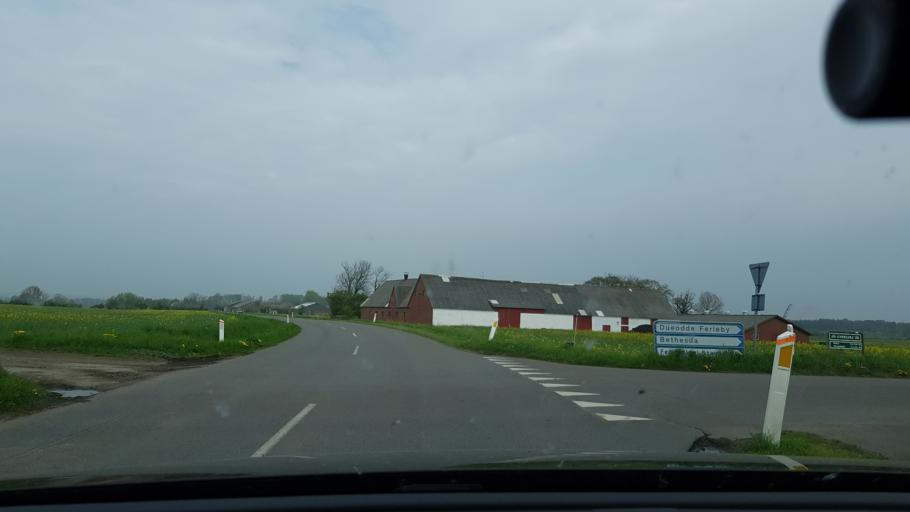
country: DK
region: Capital Region
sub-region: Bornholm Kommune
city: Nexo
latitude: 55.0103
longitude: 15.0954
